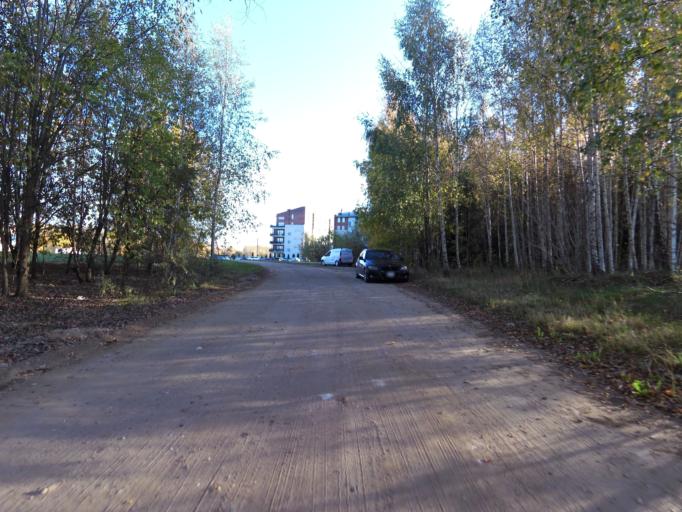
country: LT
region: Vilnius County
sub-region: Vilnius
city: Fabijoniskes
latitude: 54.7431
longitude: 25.2611
